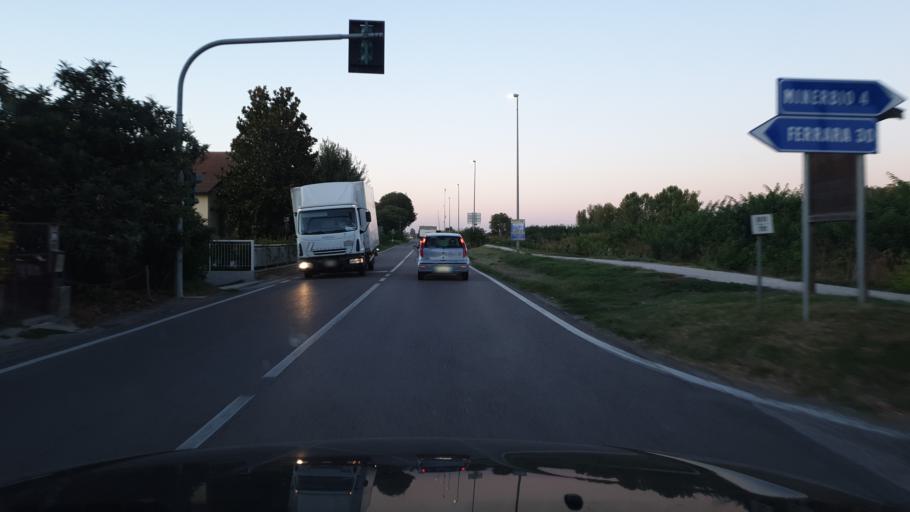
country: IT
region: Emilia-Romagna
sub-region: Provincia di Bologna
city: Ca De Fabbri
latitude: 44.6198
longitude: 11.4542
